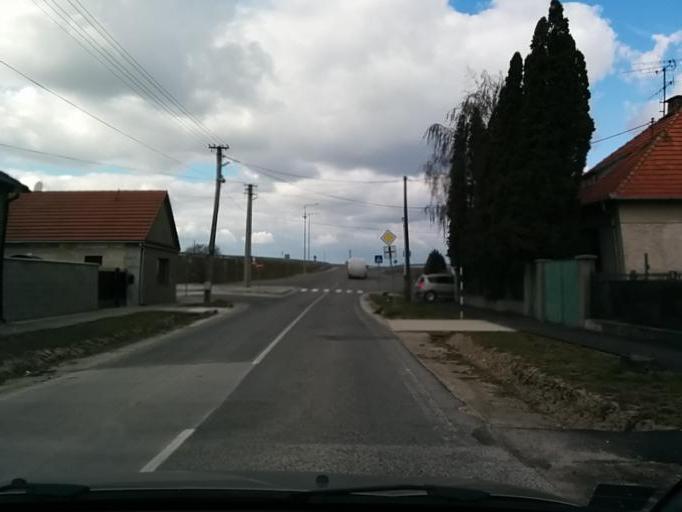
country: SK
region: Trnavsky
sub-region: Okres Trnava
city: Trnava
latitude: 48.3141
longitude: 17.6473
